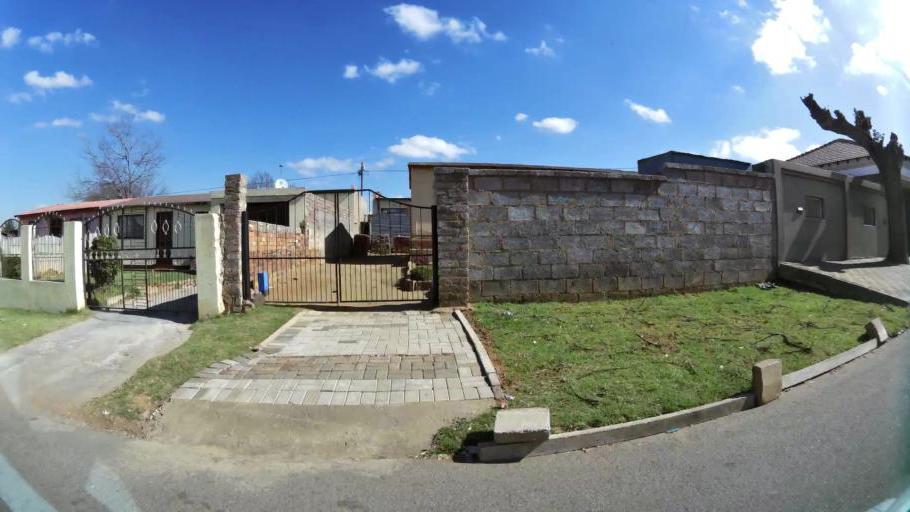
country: ZA
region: Gauteng
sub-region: City of Johannesburg Metropolitan Municipality
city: Soweto
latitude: -26.2216
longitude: 27.9120
